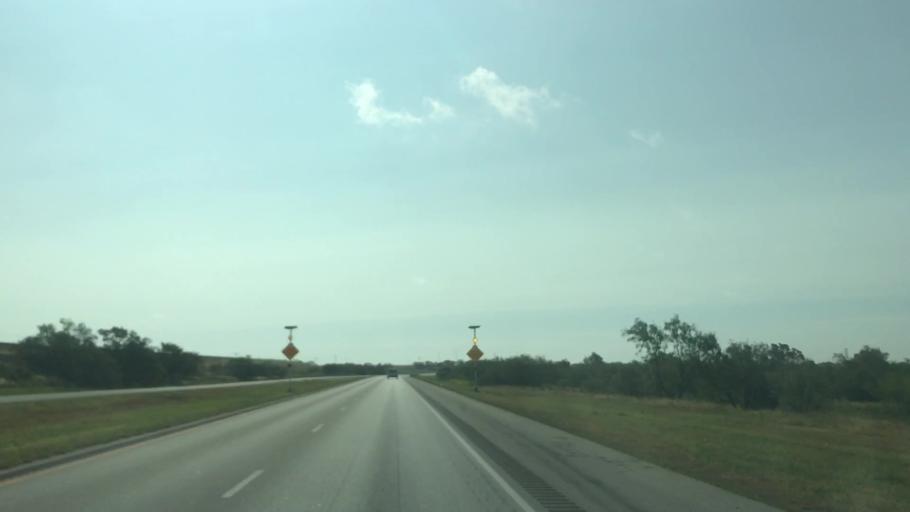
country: US
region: Texas
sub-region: Scurry County
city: Snyder
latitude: 32.6790
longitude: -100.8159
